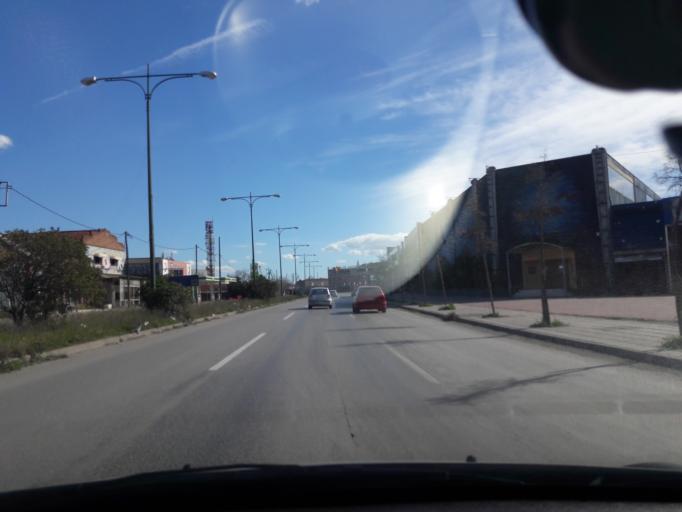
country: GR
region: Central Macedonia
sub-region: Nomos Thessalonikis
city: Menemeni
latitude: 40.6459
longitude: 22.9086
